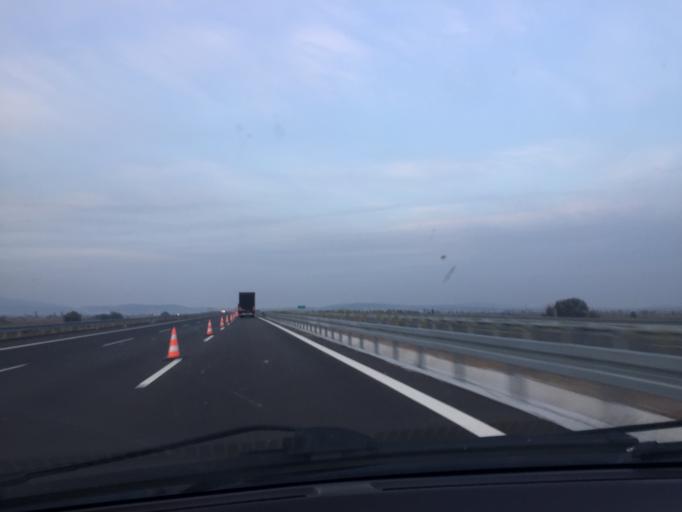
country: TR
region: Manisa
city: Halitpasa
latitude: 38.7269
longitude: 27.6541
